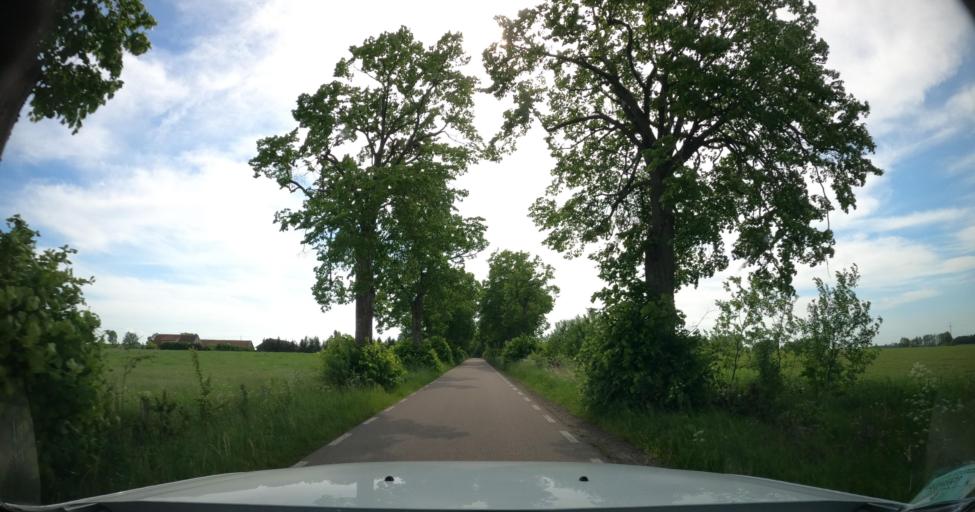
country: PL
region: Warmian-Masurian Voivodeship
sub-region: Powiat lidzbarski
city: Orneta
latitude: 54.0547
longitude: 20.1686
